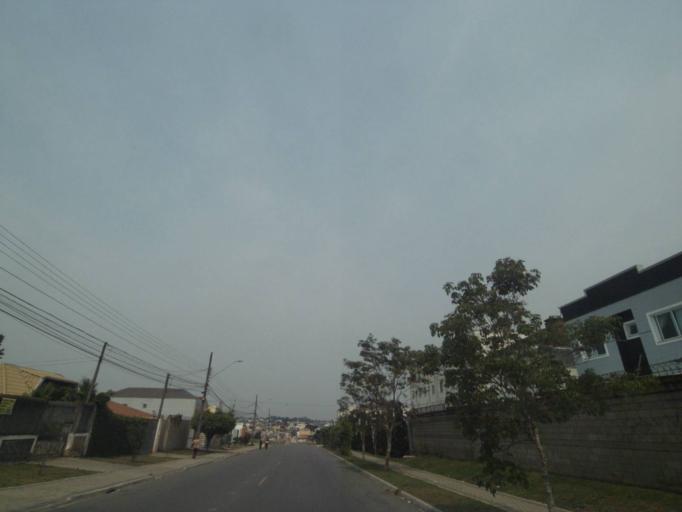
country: BR
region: Parana
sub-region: Sao Jose Dos Pinhais
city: Sao Jose dos Pinhais
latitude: -25.5159
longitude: -49.2824
